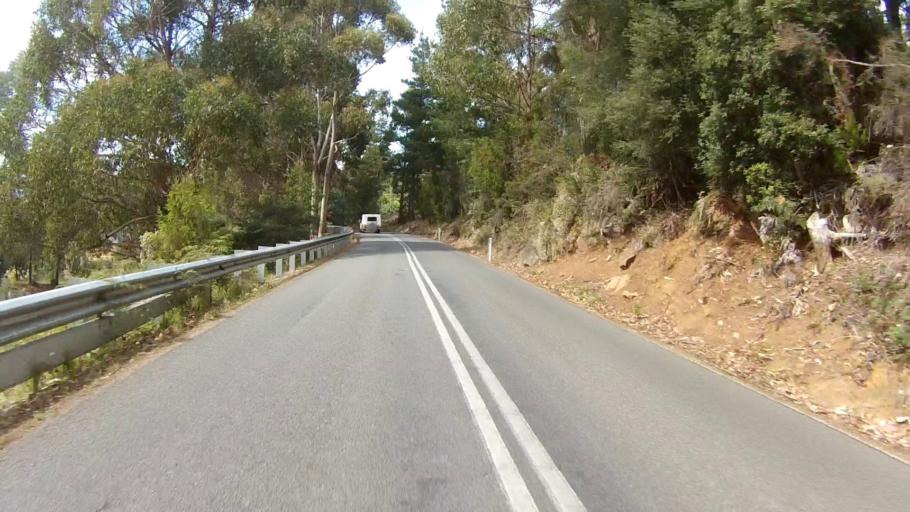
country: AU
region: Tasmania
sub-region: Kingborough
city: Kettering
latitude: -43.2034
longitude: 147.2541
